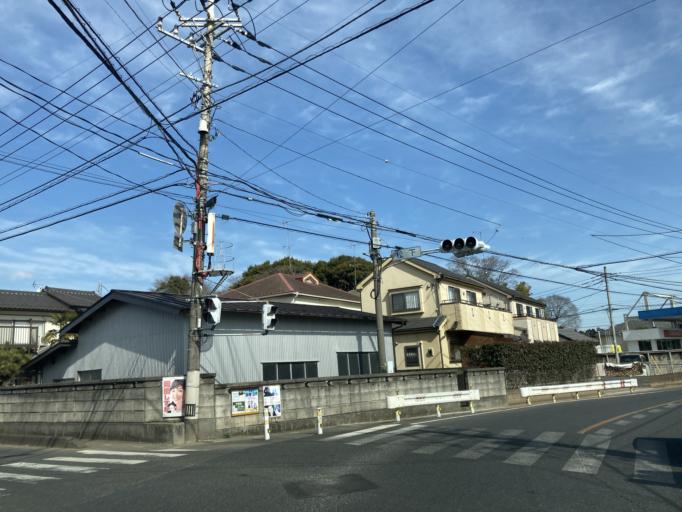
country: JP
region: Saitama
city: Tokorozawa
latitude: 35.8161
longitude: 139.4836
